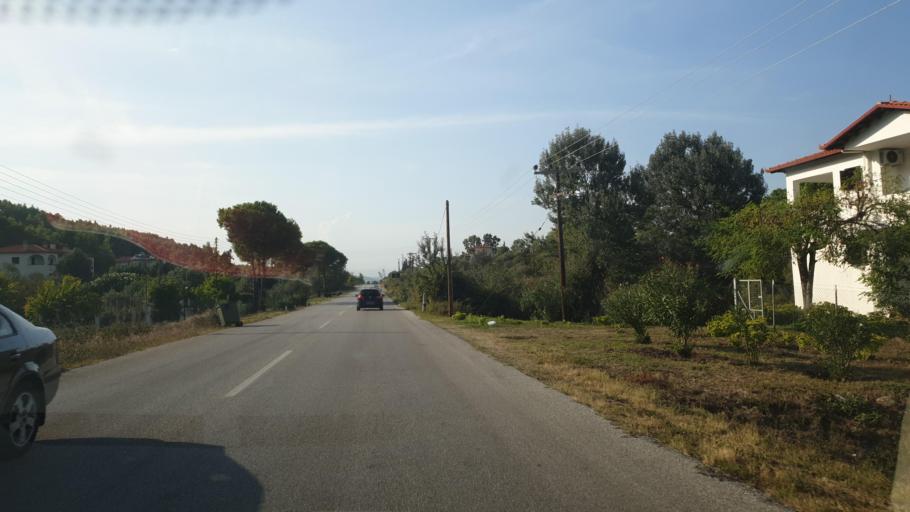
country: GR
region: Central Macedonia
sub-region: Nomos Chalkidikis
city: Agios Nikolaos
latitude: 40.2209
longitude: 23.7482
